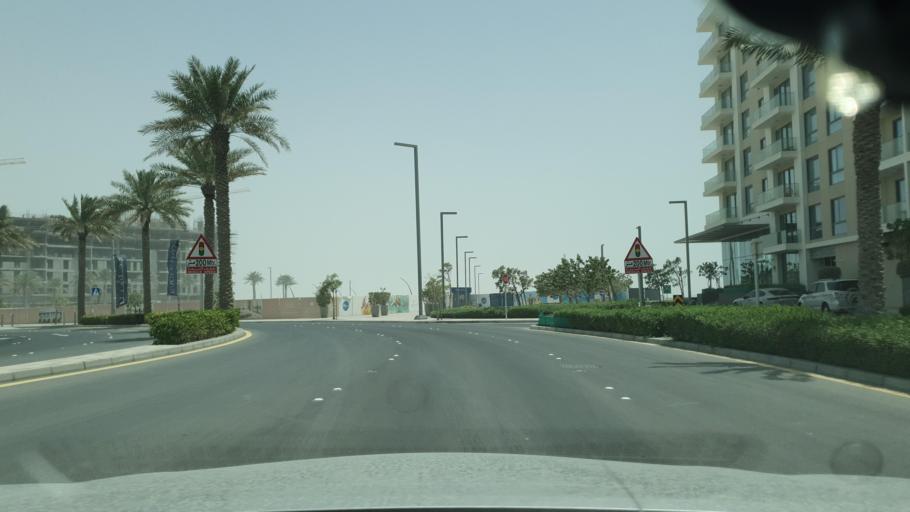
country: BH
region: Muharraq
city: Al Muharraq
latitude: 26.3054
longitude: 50.6459
